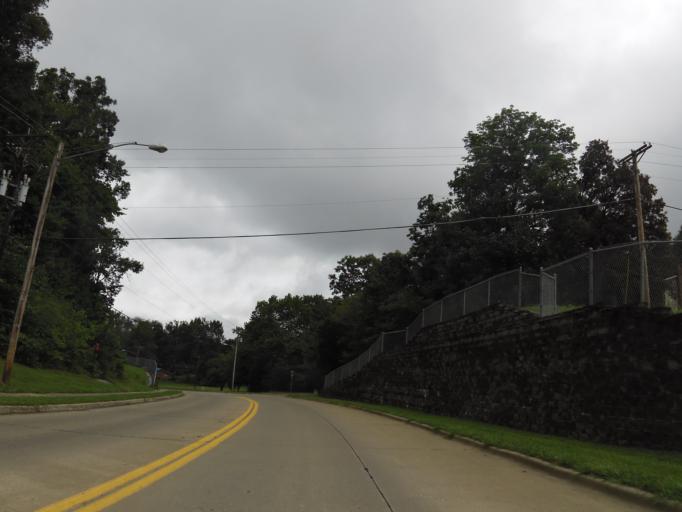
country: US
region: Missouri
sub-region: Cape Girardeau County
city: Cape Girardeau
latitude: 37.3480
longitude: -89.5592
